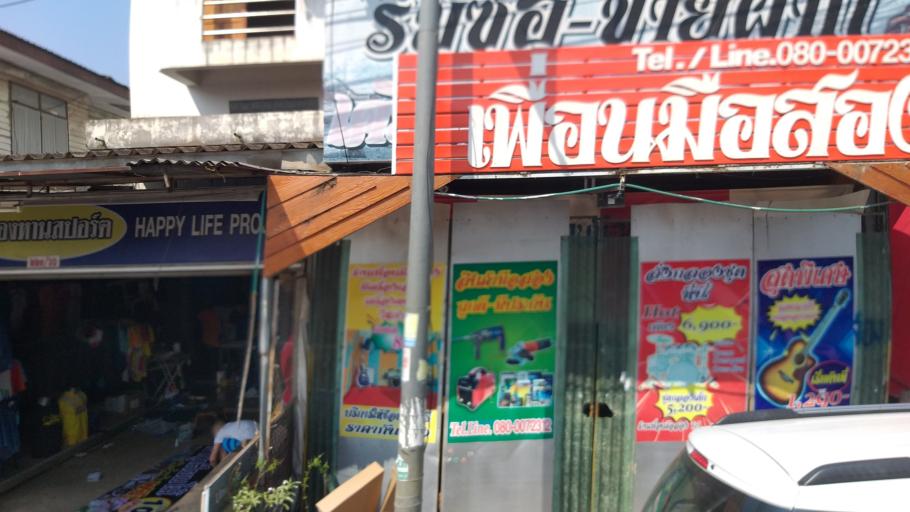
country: TH
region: Changwat Udon Thani
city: Nong Han
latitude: 17.3633
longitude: 103.1096
